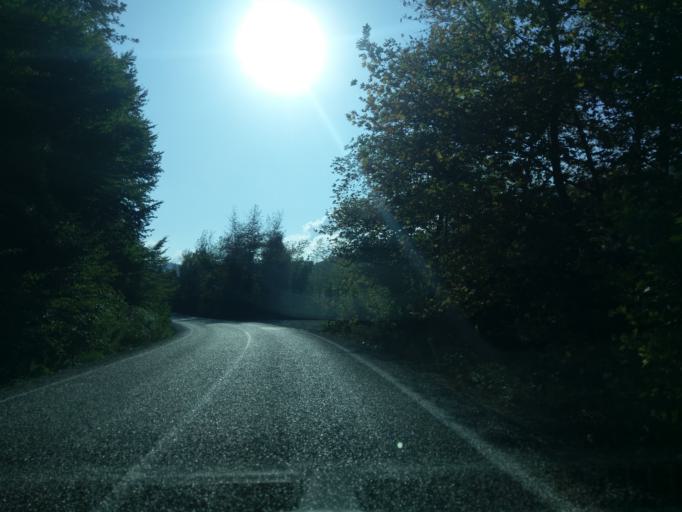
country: TR
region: Sinop
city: Yenikonak
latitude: 41.8821
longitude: 34.5609
